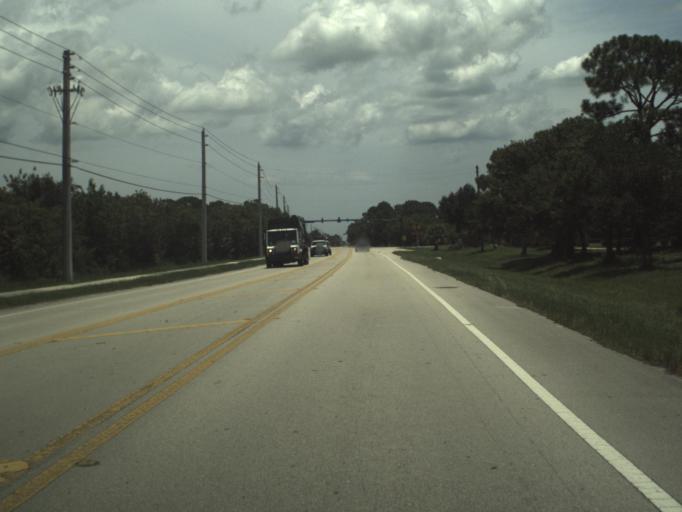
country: US
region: Florida
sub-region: Martin County
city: Port Salerno
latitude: 27.1206
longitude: -80.2410
